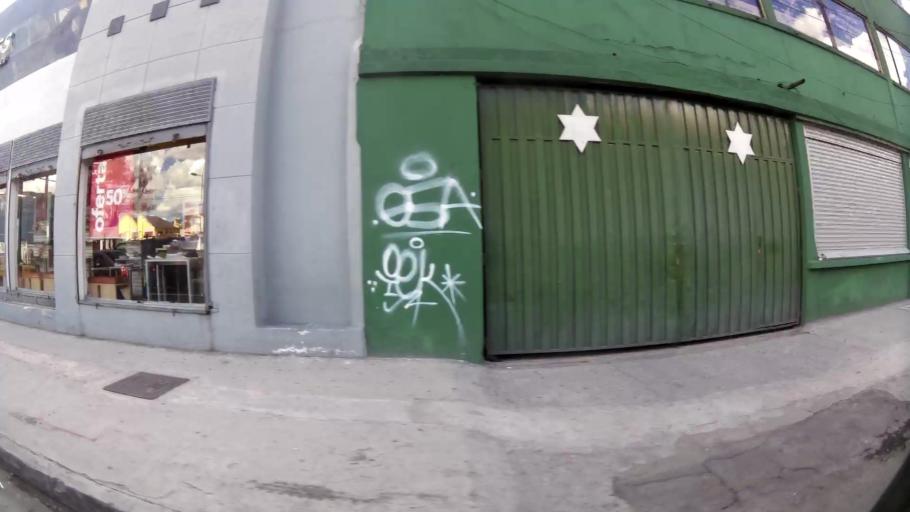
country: EC
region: Pichincha
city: Quito
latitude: -0.1978
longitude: -78.4960
